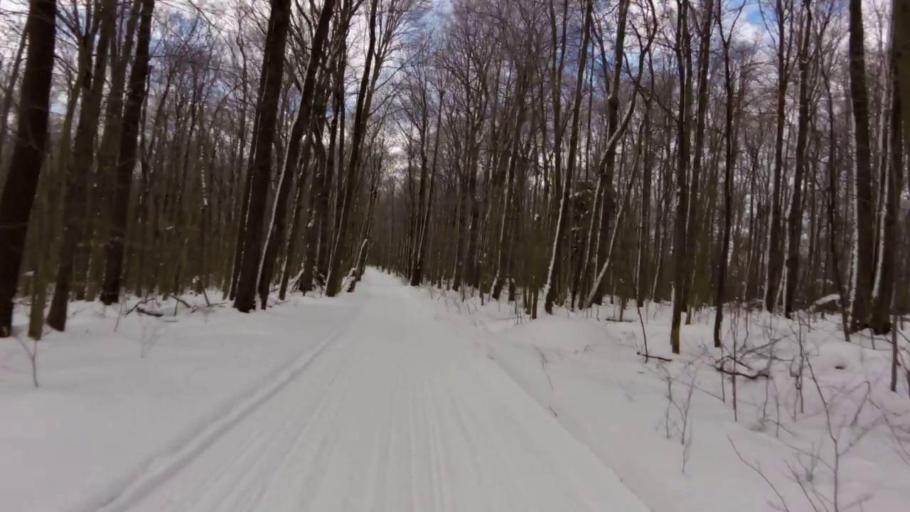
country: US
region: New York
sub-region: Cattaraugus County
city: Salamanca
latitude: 42.0471
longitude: -78.7578
